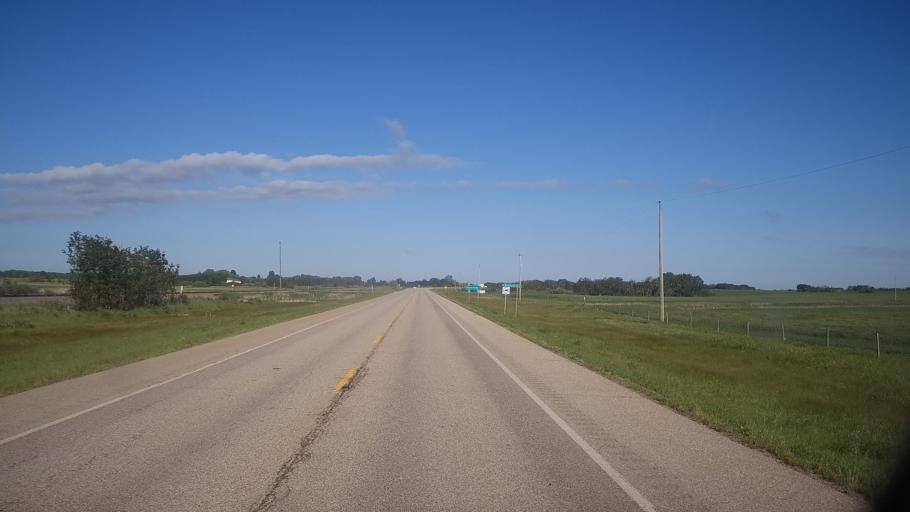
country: CA
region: Saskatchewan
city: Lanigan
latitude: 51.8699
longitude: -105.1657
